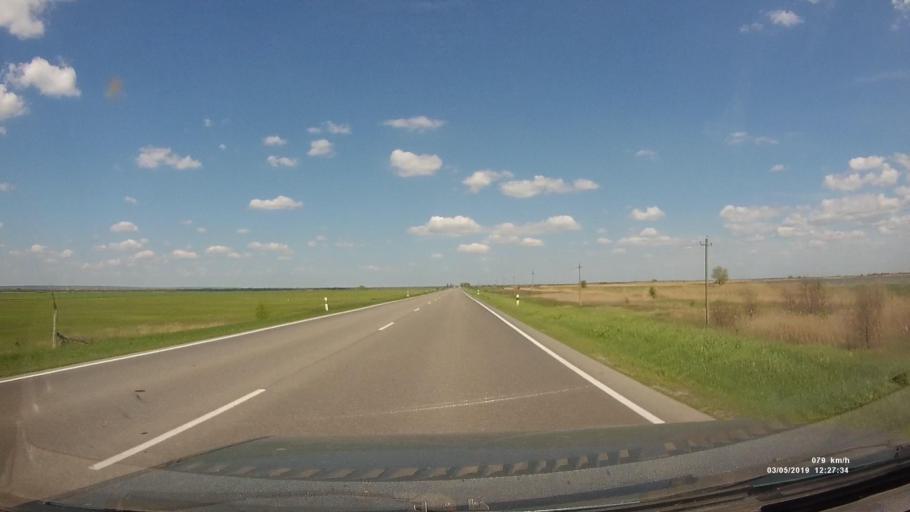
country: RU
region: Rostov
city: Semikarakorsk
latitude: 47.4610
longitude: 40.7218
